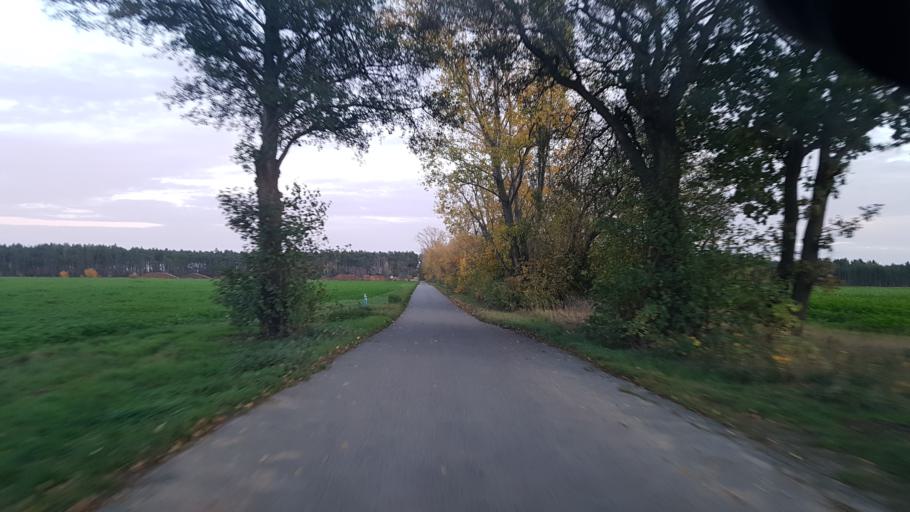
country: DE
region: Brandenburg
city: Bad Liebenwerda
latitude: 51.5119
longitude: 13.3105
